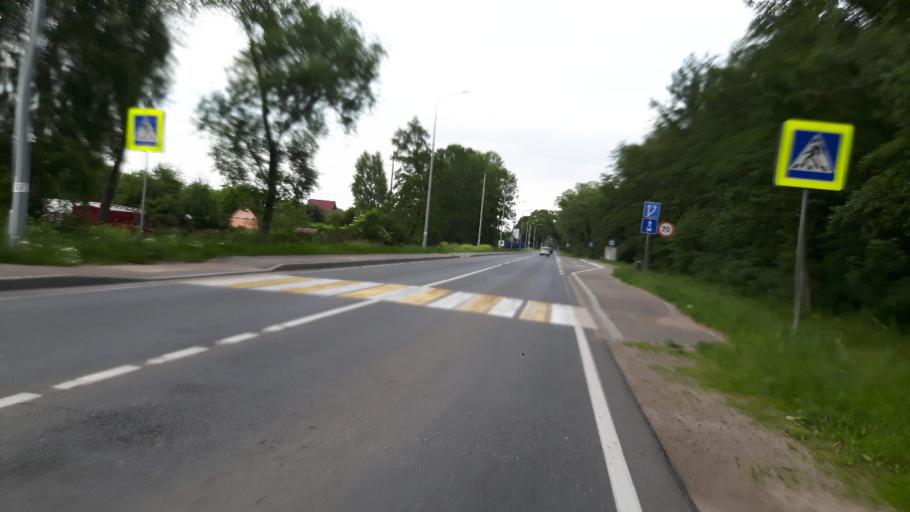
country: RU
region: Kaliningrad
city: Vzmorye
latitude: 54.6414
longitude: 20.3410
